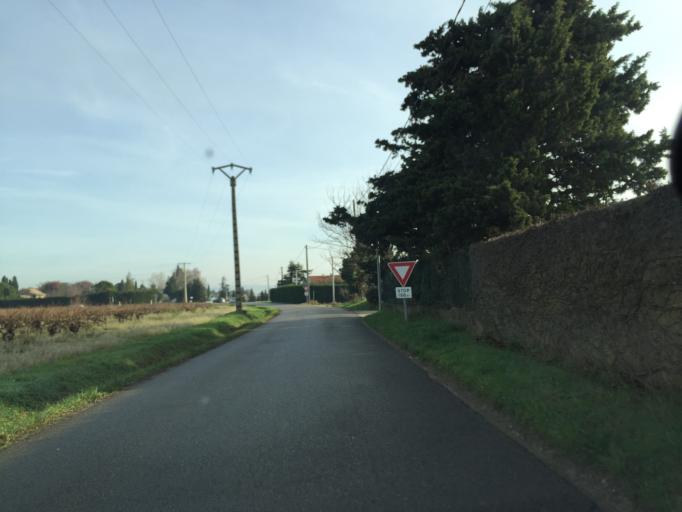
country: FR
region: Provence-Alpes-Cote d'Azur
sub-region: Departement du Vaucluse
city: Serignan-du-Comtat
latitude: 44.1712
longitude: 4.8543
